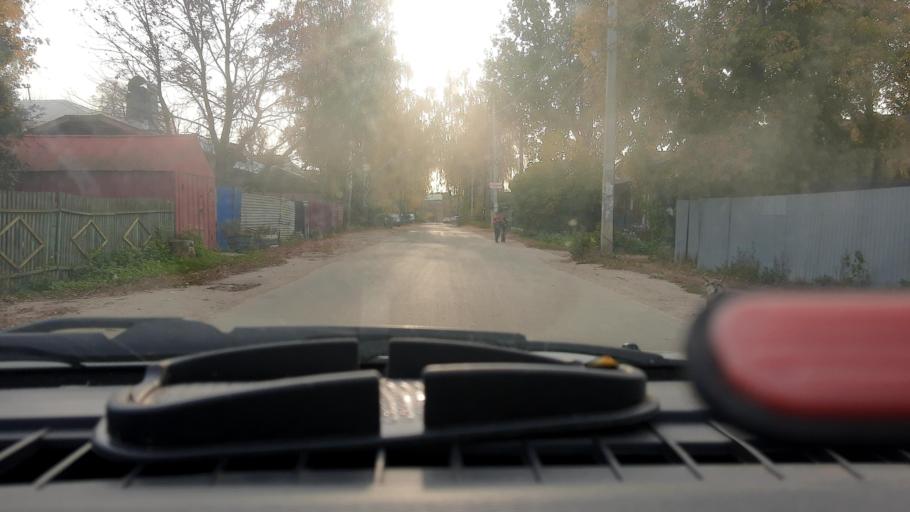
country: RU
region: Nizjnij Novgorod
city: Nizhniy Novgorod
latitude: 56.3070
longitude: 43.9113
